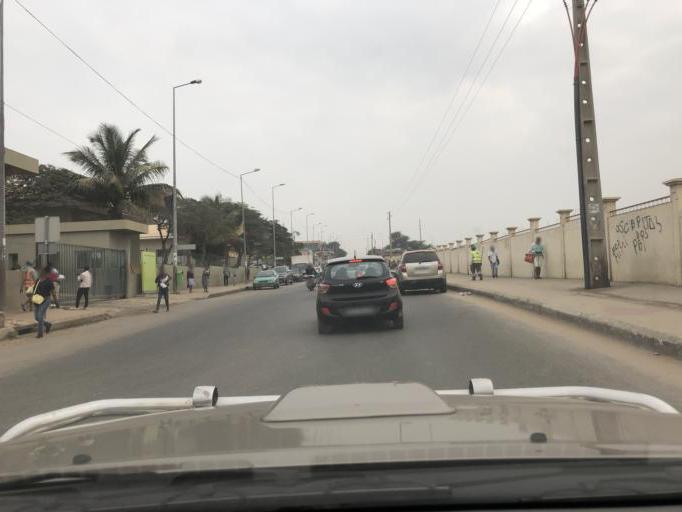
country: AO
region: Luanda
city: Luanda
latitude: -8.9021
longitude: 13.2153
